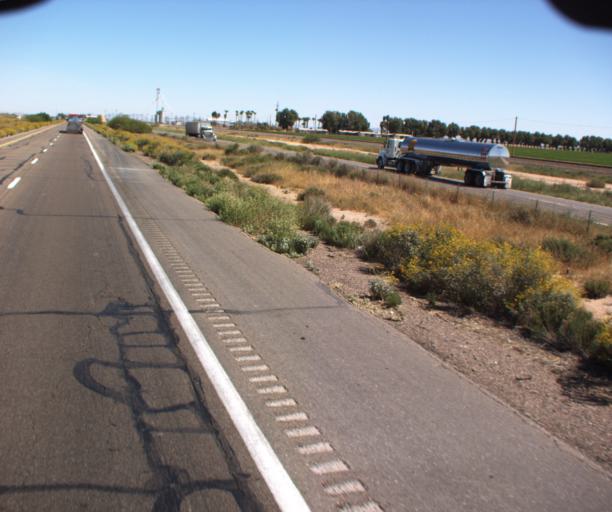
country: US
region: Arizona
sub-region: Maricopa County
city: Gila Bend
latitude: 32.9192
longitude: -112.9001
